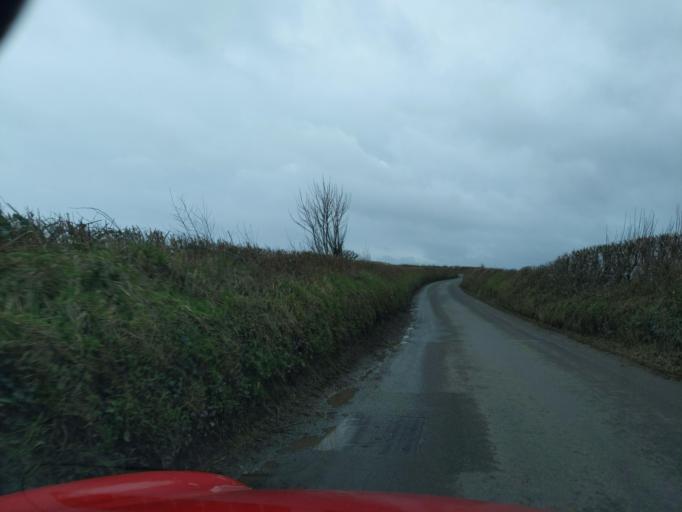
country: GB
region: England
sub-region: Devon
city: Modbury
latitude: 50.3280
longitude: -3.8817
